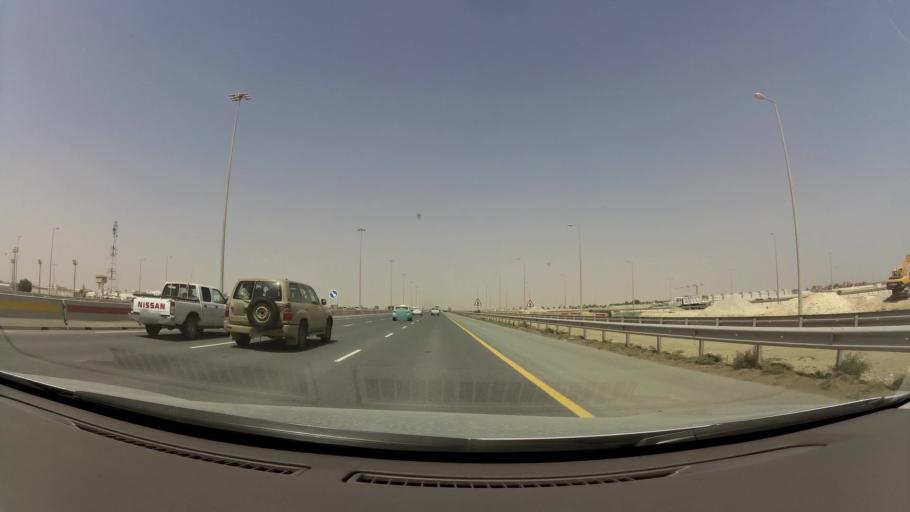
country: QA
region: Baladiyat Umm Salal
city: Umm Salal `Ali
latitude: 25.4511
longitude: 51.4099
